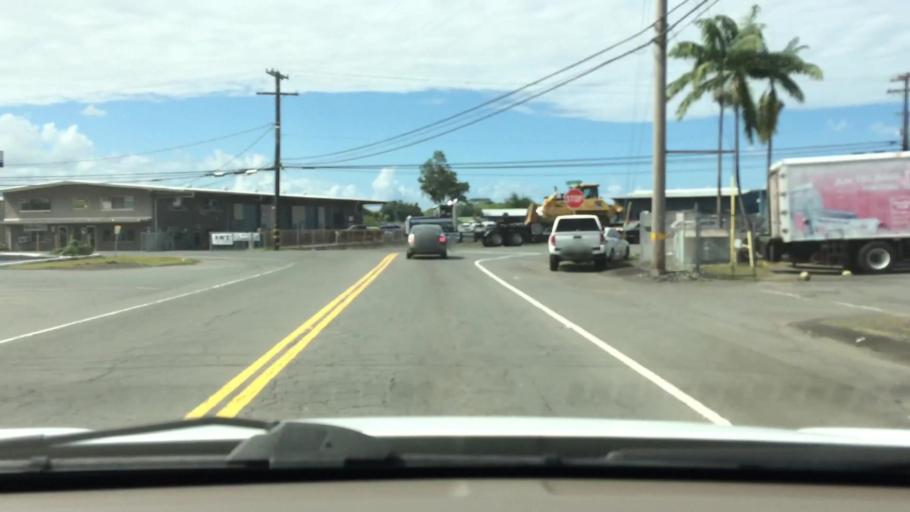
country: US
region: Hawaii
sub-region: Hawaii County
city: Hilo
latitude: 19.7091
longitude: -155.0618
